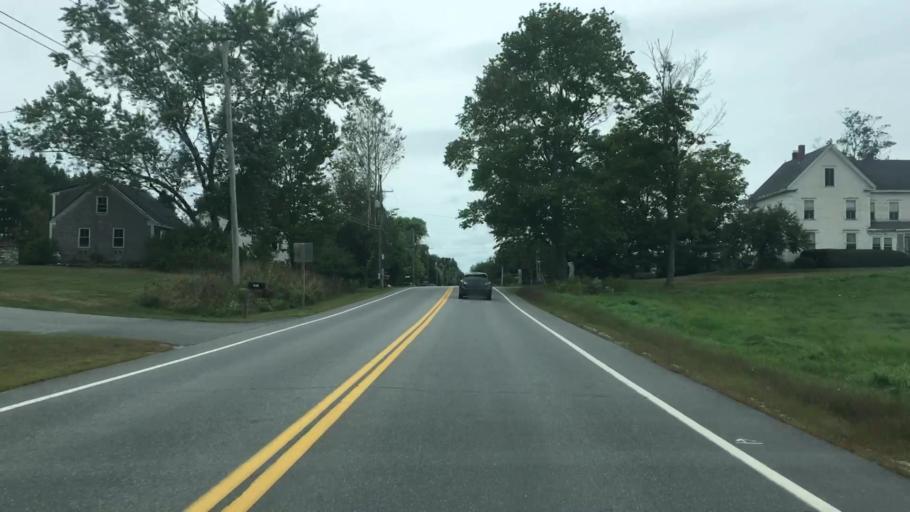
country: US
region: Maine
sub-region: Cumberland County
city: Yarmouth
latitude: 43.8184
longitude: -70.1854
